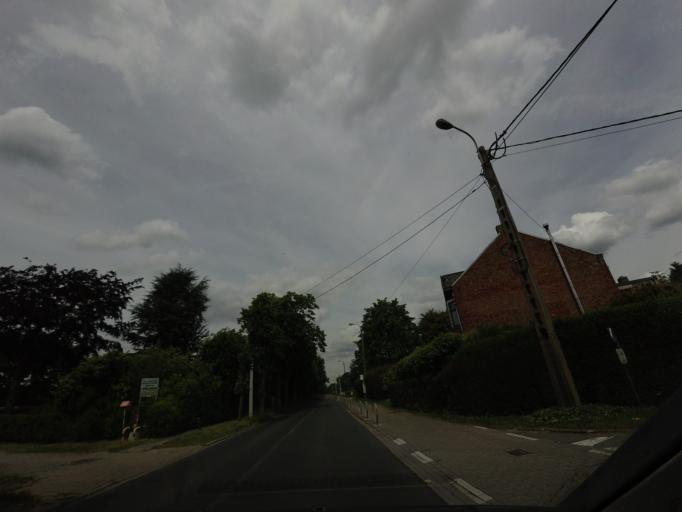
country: BE
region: Flanders
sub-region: Provincie Antwerpen
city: Bornem
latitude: 51.0946
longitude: 4.2677
